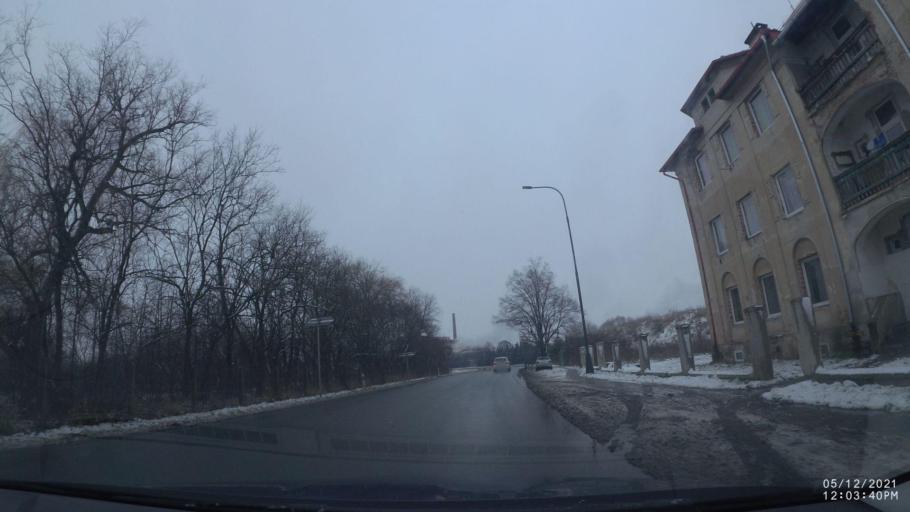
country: CZ
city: Ceske Mezirici
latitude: 50.2833
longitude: 16.0572
